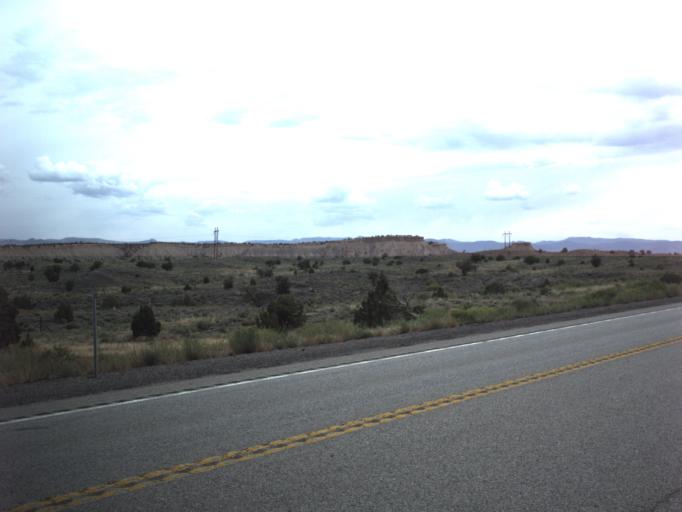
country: US
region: Utah
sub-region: Carbon County
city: Wellington
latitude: 39.5469
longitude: -110.6415
